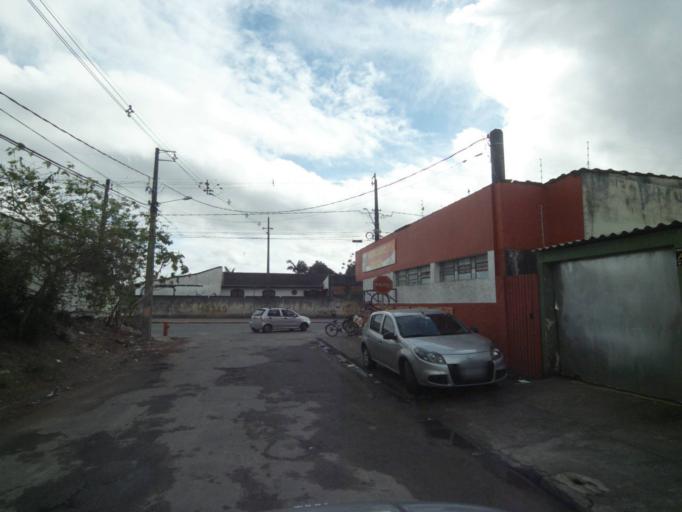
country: BR
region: Parana
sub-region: Paranagua
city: Paranagua
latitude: -25.5697
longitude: -48.5625
